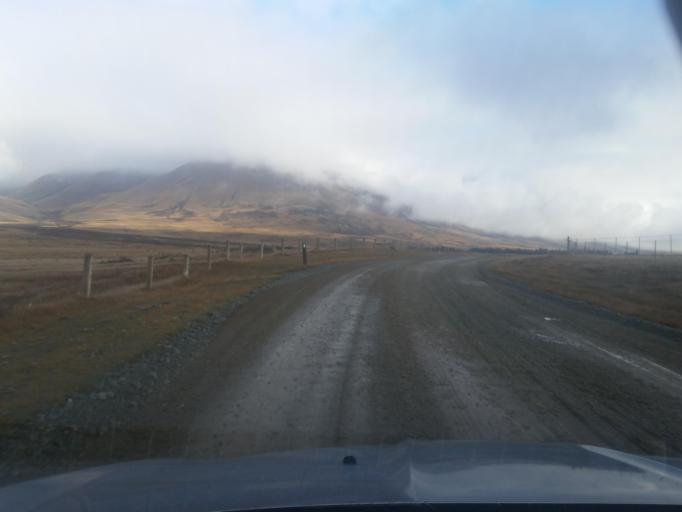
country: NZ
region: Canterbury
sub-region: Ashburton District
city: Methven
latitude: -43.6167
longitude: 171.0850
